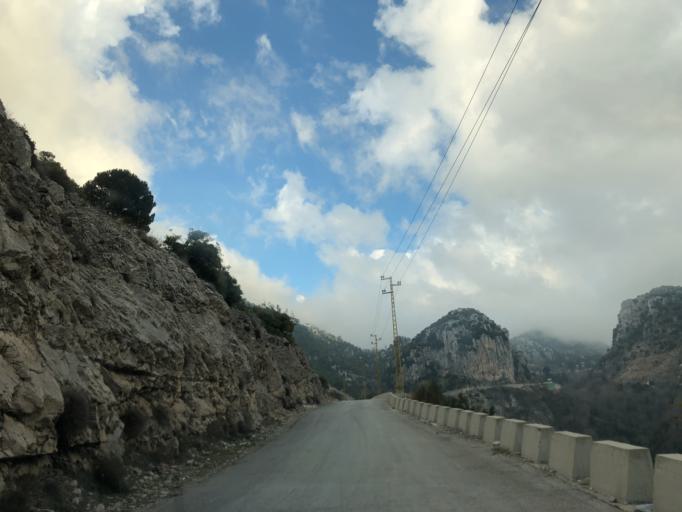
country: LB
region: Liban-Nord
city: Amioun
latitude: 34.1989
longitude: 35.8862
